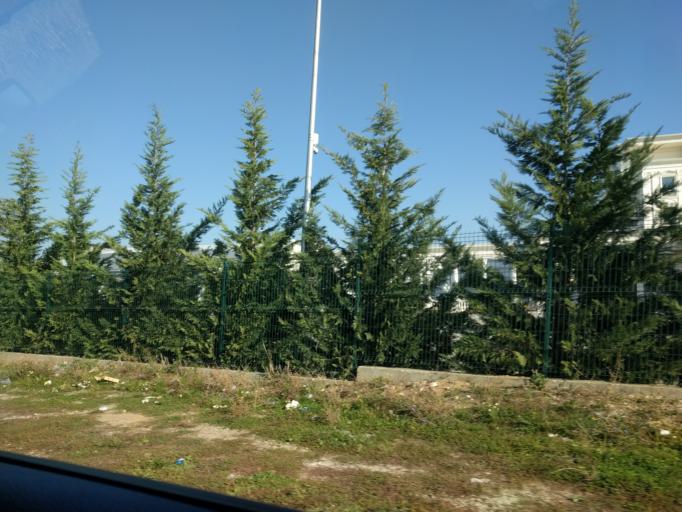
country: XK
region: Prizren
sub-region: Prizren
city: Prizren
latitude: 42.2412
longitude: 20.7526
